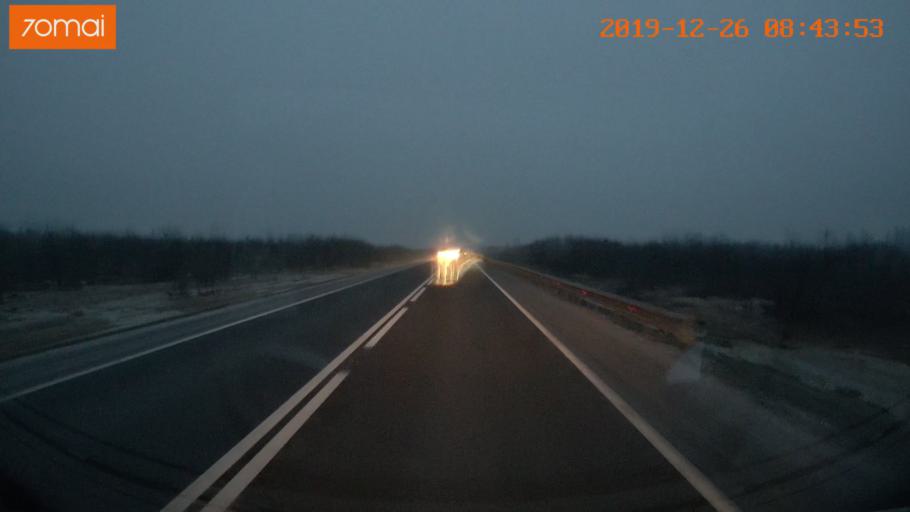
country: RU
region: Jaroslavl
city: Prechistoye
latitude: 58.5784
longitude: 40.3514
